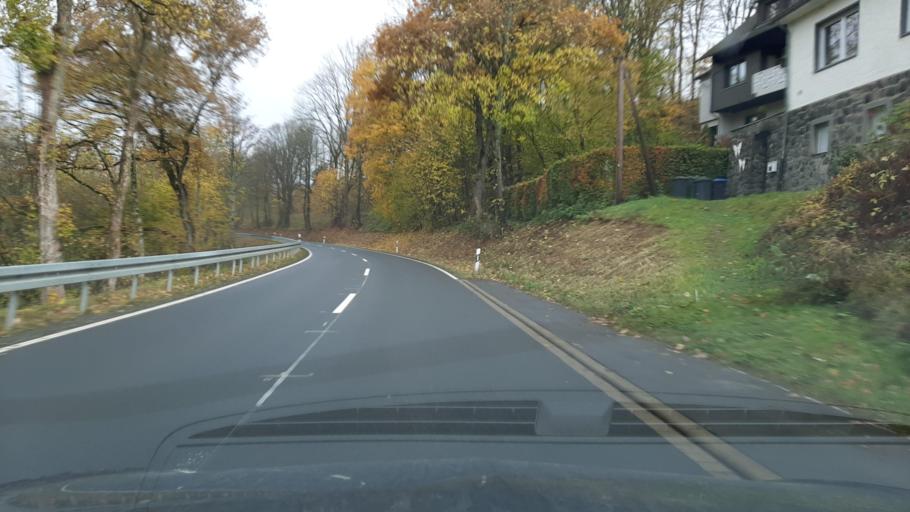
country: DE
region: North Rhine-Westphalia
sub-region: Regierungsbezirk Arnsberg
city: Winterberg
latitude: 51.2569
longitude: 8.4723
